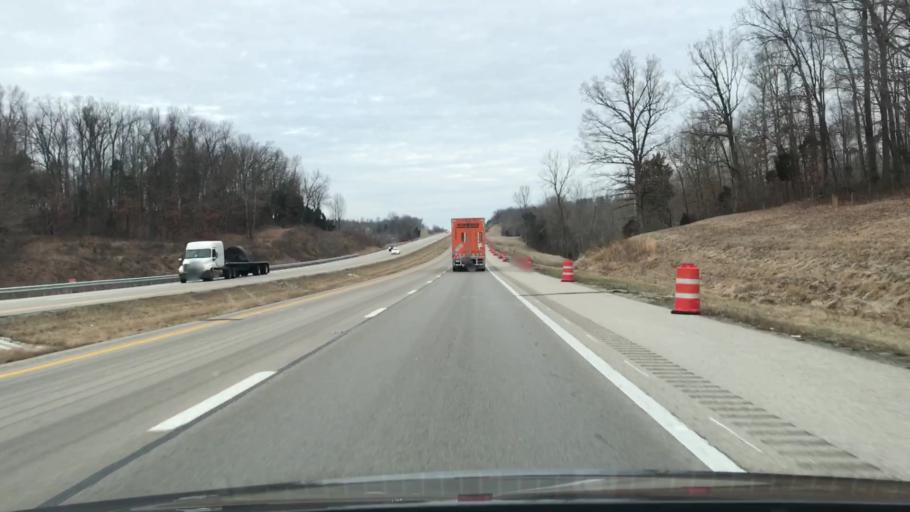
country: US
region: Kentucky
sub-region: Ohio County
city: Hartford
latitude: 37.5147
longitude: -86.9171
